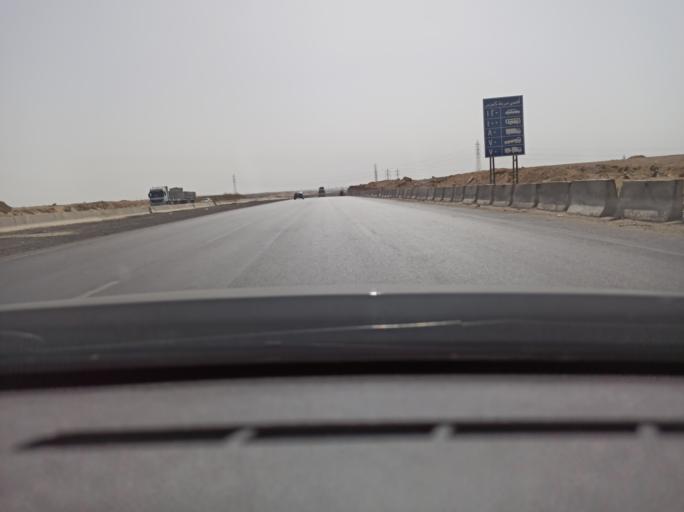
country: EG
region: Muhafazat al Qahirah
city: Halwan
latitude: 29.7859
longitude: 31.3536
